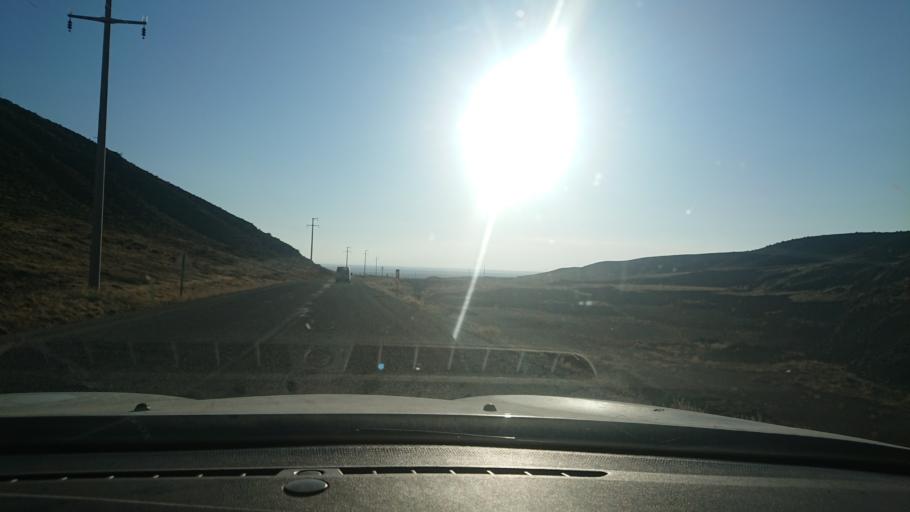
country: TR
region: Aksaray
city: Acipinar
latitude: 38.6867
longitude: 33.7409
